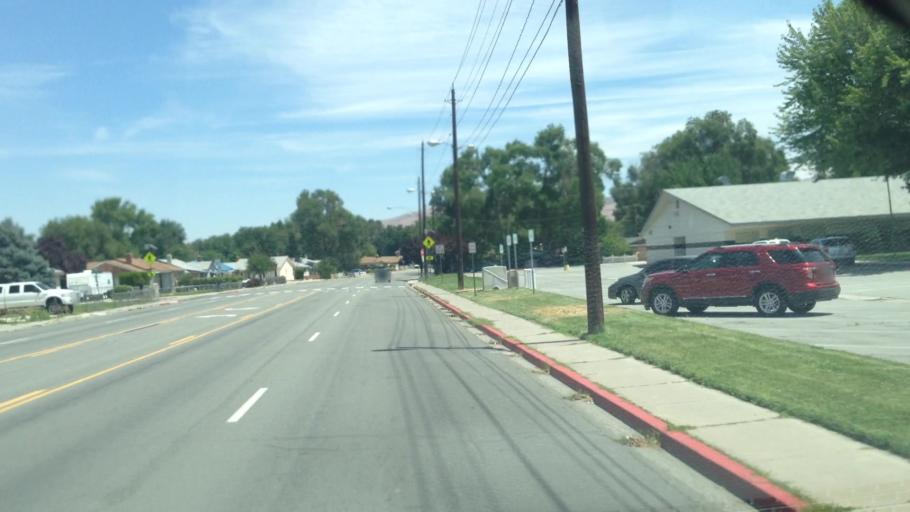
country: US
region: Nevada
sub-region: Washoe County
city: Sparks
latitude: 39.5415
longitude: -119.7461
